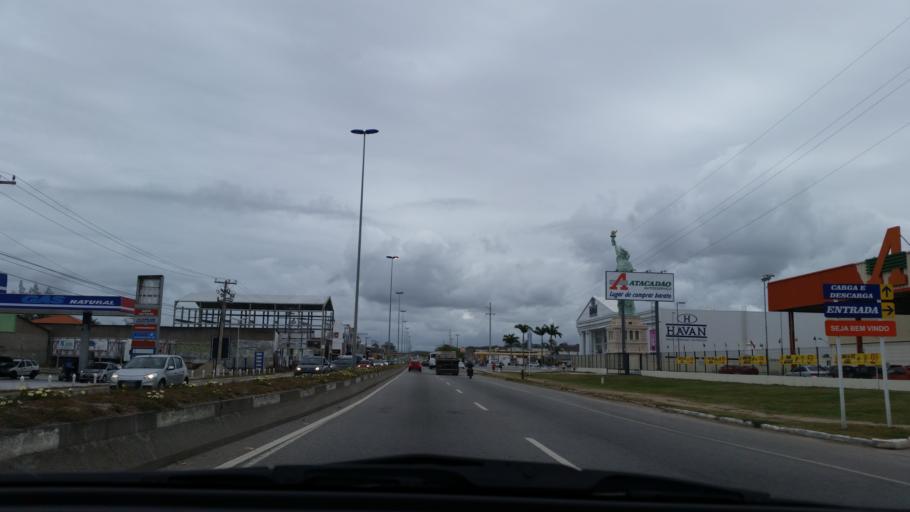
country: BR
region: Rio de Janeiro
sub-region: Sao Pedro Da Aldeia
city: Sao Pedro da Aldeia
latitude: -22.8438
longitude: -42.0693
